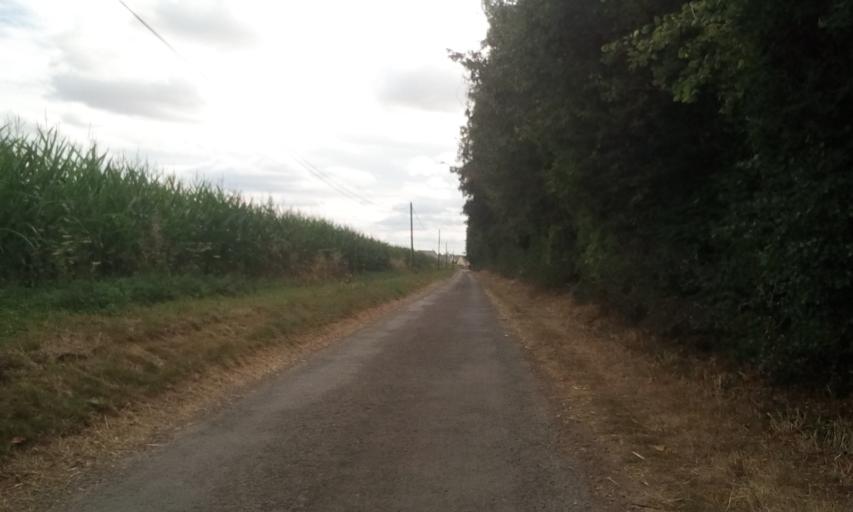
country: FR
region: Lower Normandy
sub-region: Departement du Calvados
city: Bellengreville
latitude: 49.1277
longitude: -0.1946
